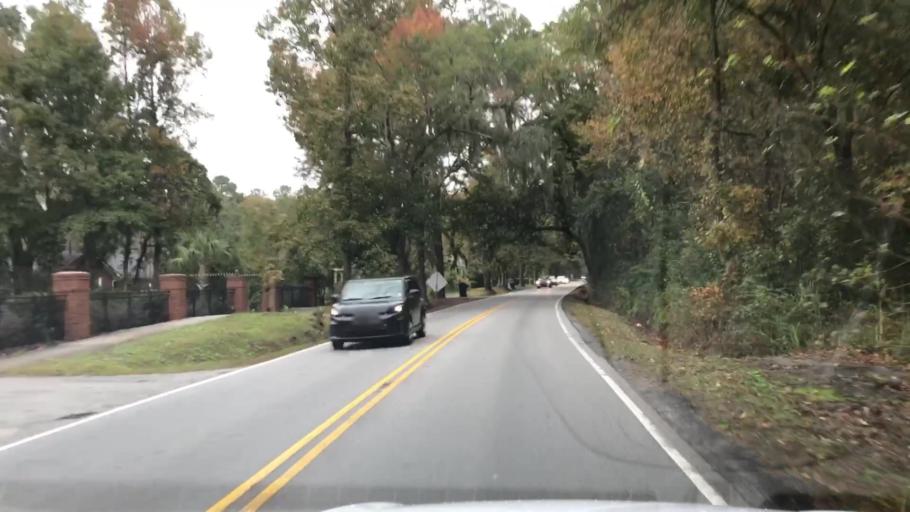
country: US
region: South Carolina
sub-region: Charleston County
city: Mount Pleasant
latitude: 32.8424
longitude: -79.8433
